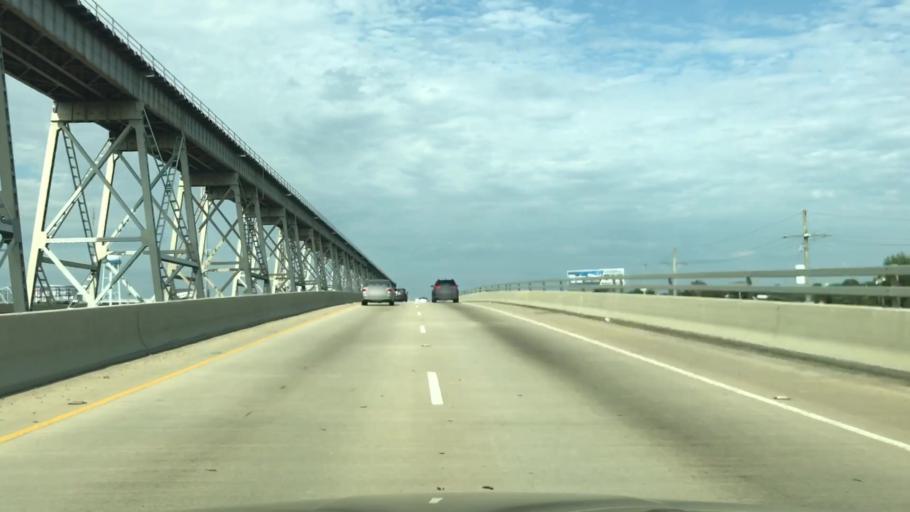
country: US
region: Louisiana
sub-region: Jefferson Parish
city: Bridge City
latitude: 29.9291
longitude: -90.1656
